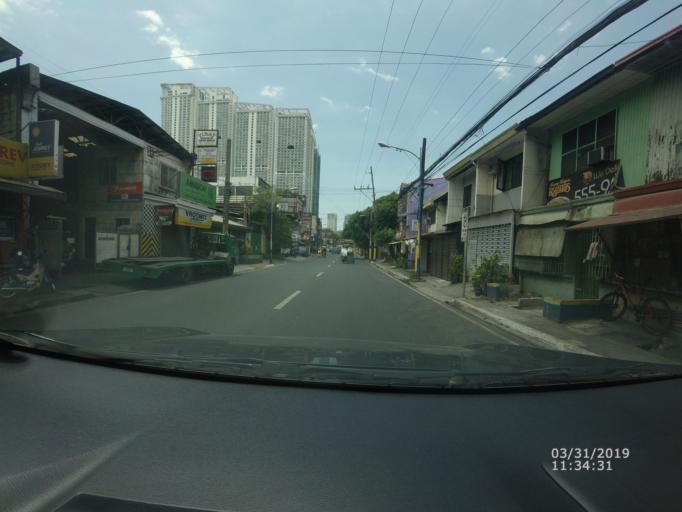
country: PH
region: Metro Manila
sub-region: Mandaluyong
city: Mandaluyong City
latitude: 14.5711
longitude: 121.0373
